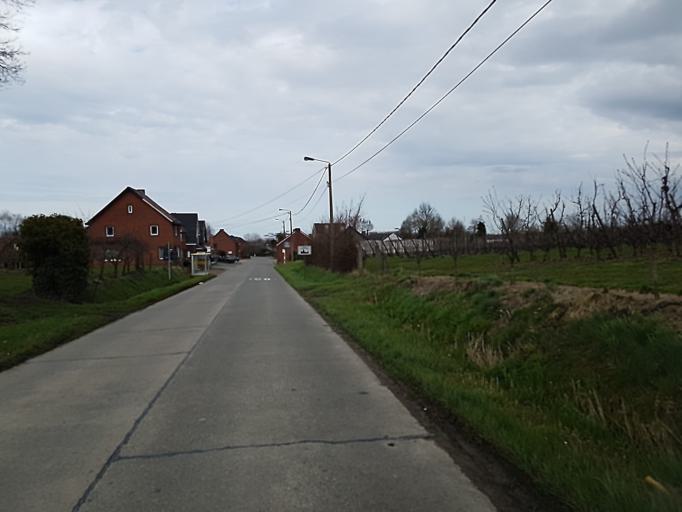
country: BE
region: Flanders
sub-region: Provincie Limburg
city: Nieuwerkerken
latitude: 50.8701
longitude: 5.2399
